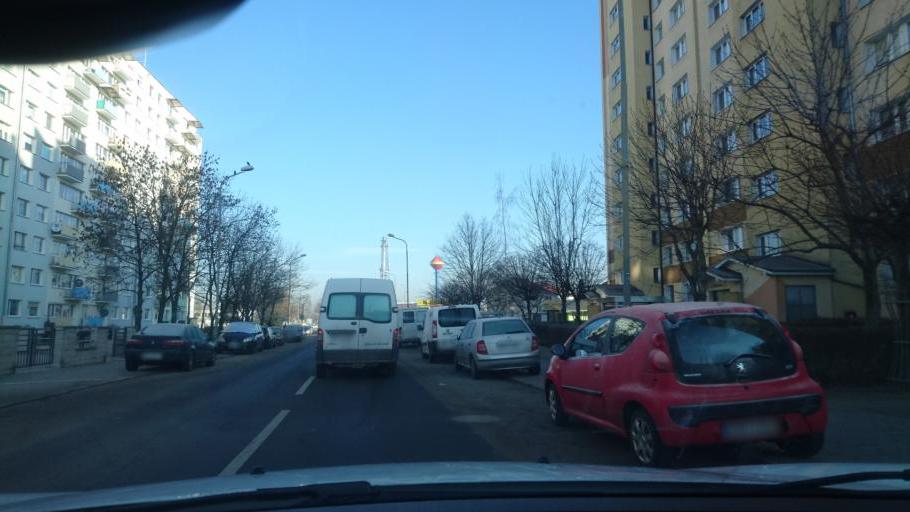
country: PL
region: Opole Voivodeship
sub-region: Powiat nyski
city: Nysa
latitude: 50.4656
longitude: 17.3399
